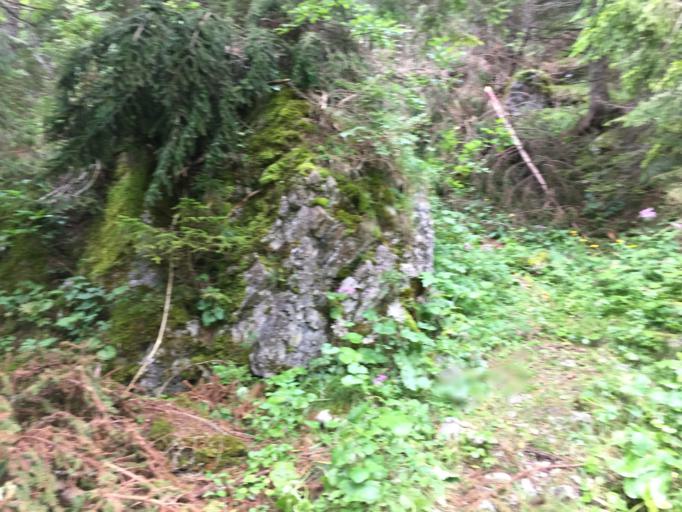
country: IT
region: Friuli Venezia Giulia
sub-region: Provincia di Udine
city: Forni Avoltri
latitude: 46.5865
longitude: 12.7353
